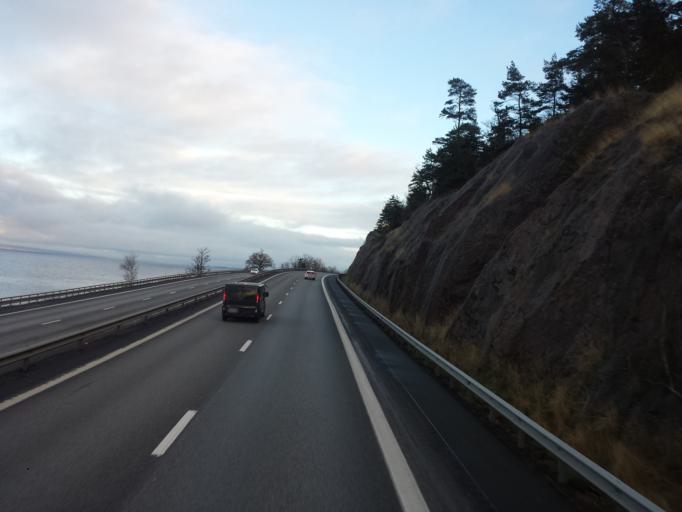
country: SE
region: Joenkoeping
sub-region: Jonkopings Kommun
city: Kaxholmen
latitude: 57.8679
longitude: 14.2711
